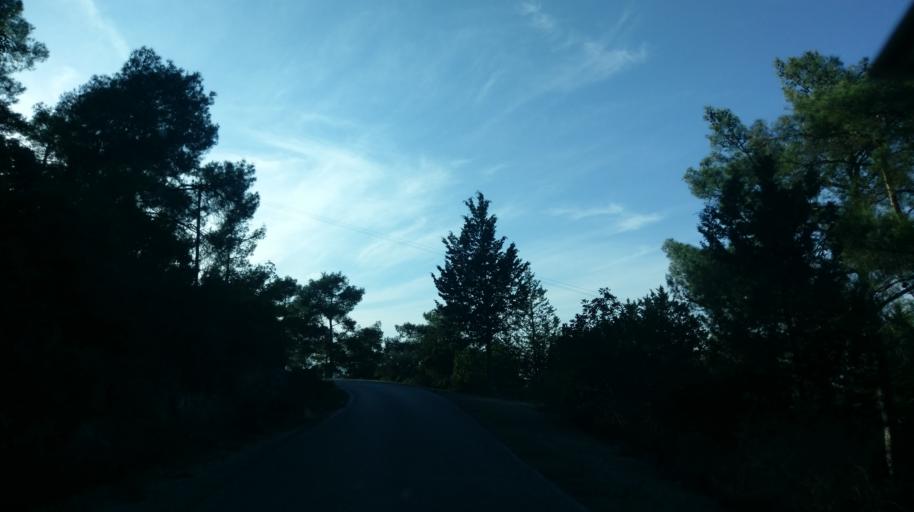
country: CY
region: Ammochostos
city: Lefkonoiko
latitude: 35.3203
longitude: 33.5896
